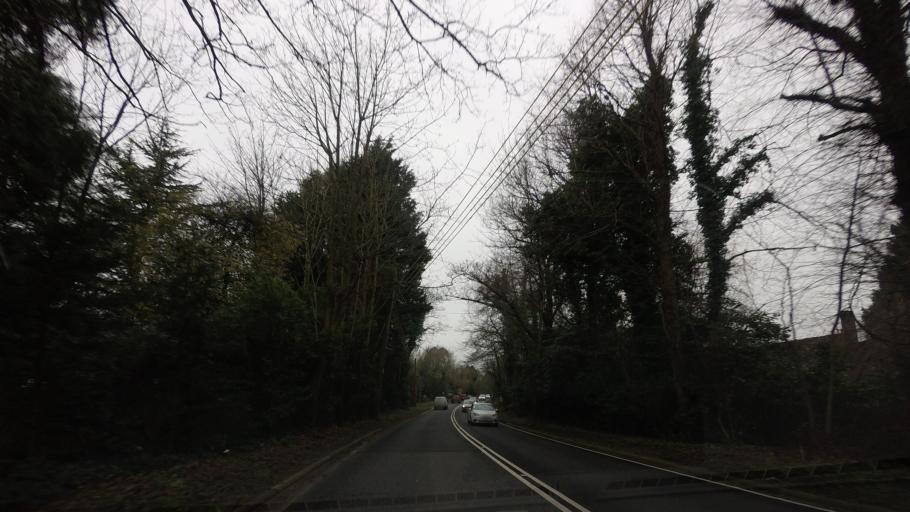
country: GB
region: England
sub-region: East Sussex
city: Battle
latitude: 50.9494
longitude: 0.5063
